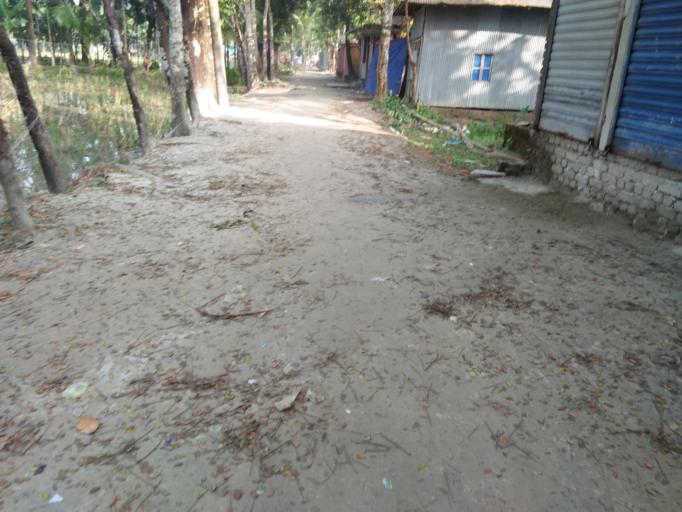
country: BD
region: Barisal
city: Bhola
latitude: 22.6776
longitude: 90.6401
